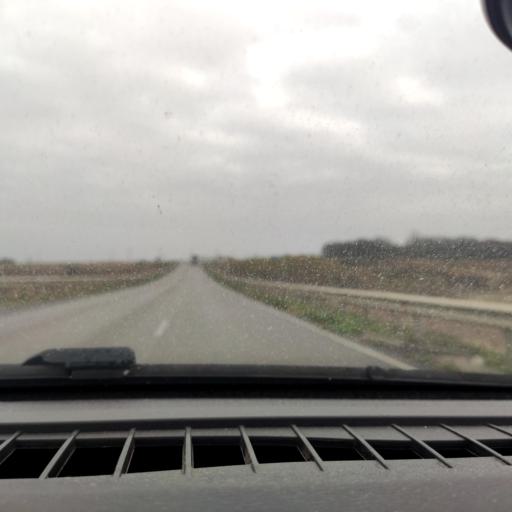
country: RU
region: Belgorod
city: Ilovka
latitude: 50.7673
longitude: 38.7523
